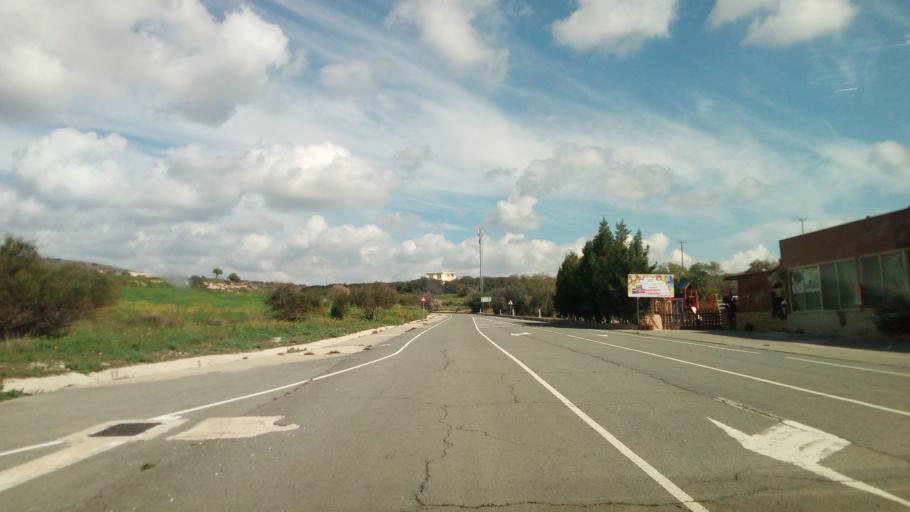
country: CY
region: Pafos
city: Mesogi
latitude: 34.7447
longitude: 32.5449
